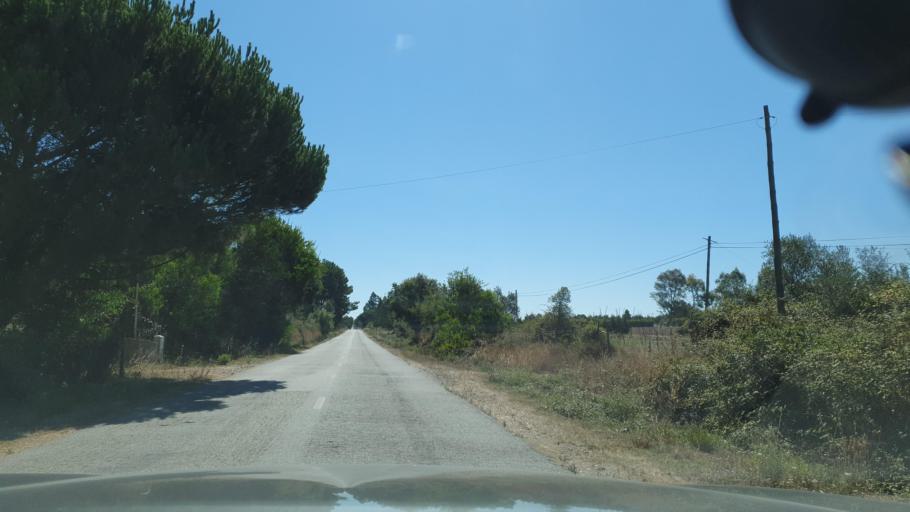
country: PT
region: Beja
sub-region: Odemira
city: Sao Teotonio
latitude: 37.4993
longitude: -8.6722
